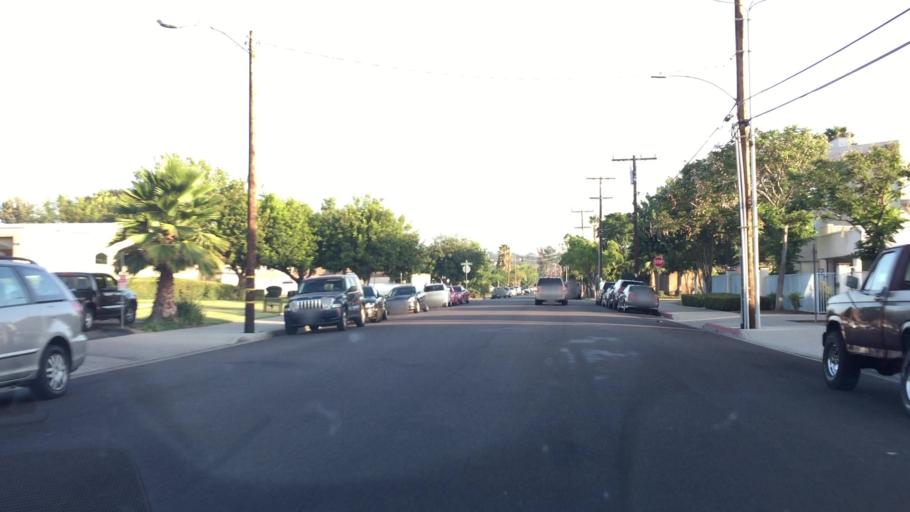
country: US
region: California
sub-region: San Diego County
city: El Cajon
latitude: 32.7935
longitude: -116.9589
